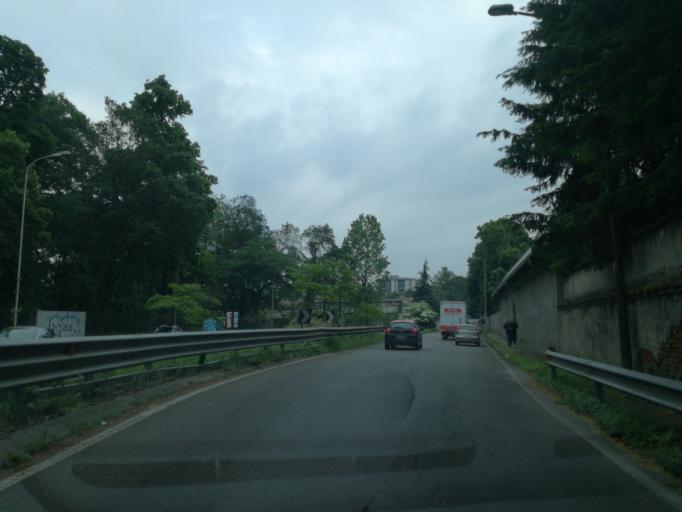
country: IT
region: Lombardy
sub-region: Provincia di Monza e Brianza
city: Monza
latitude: 45.5914
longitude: 9.2794
